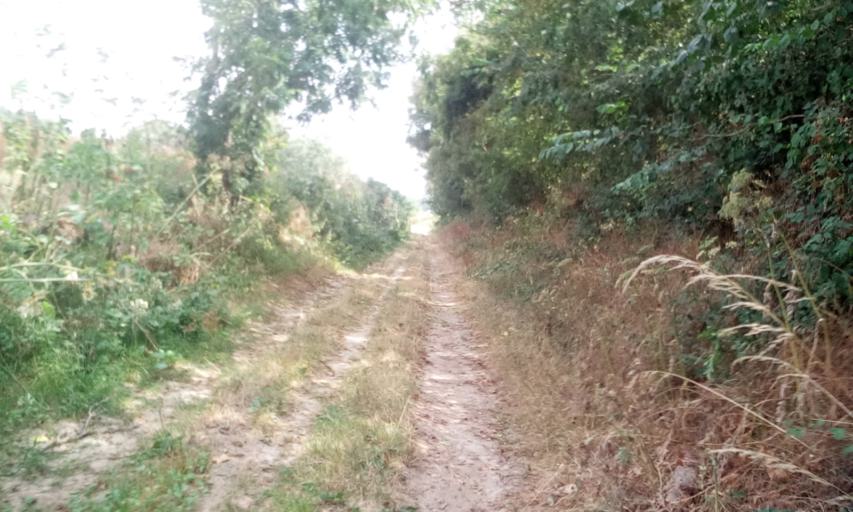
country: FR
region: Lower Normandy
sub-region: Departement du Calvados
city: Douvres-la-Delivrande
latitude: 49.2933
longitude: -0.3960
